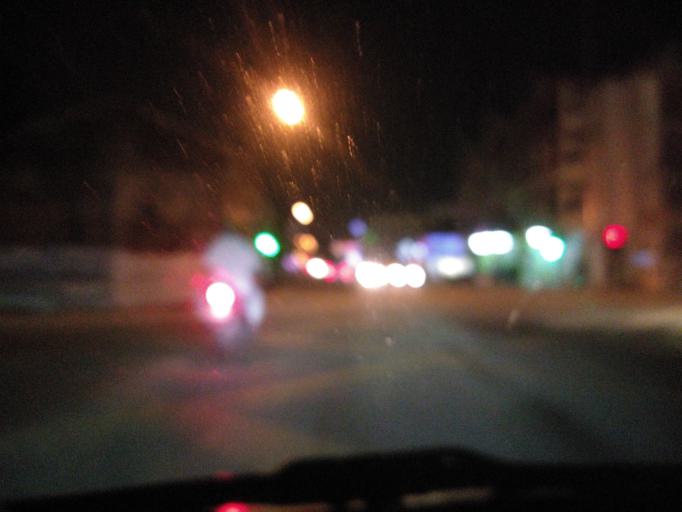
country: MY
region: Penang
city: Butterworth
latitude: 5.4130
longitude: 100.3719
